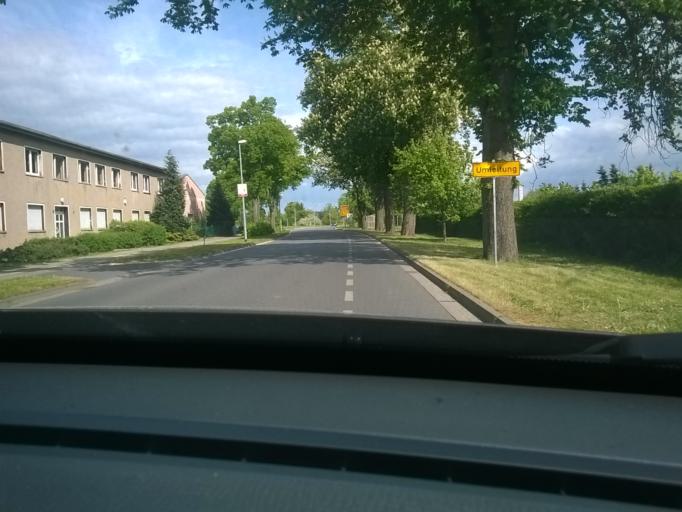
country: DE
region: Brandenburg
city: Wittstock
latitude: 53.1621
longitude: 12.5004
